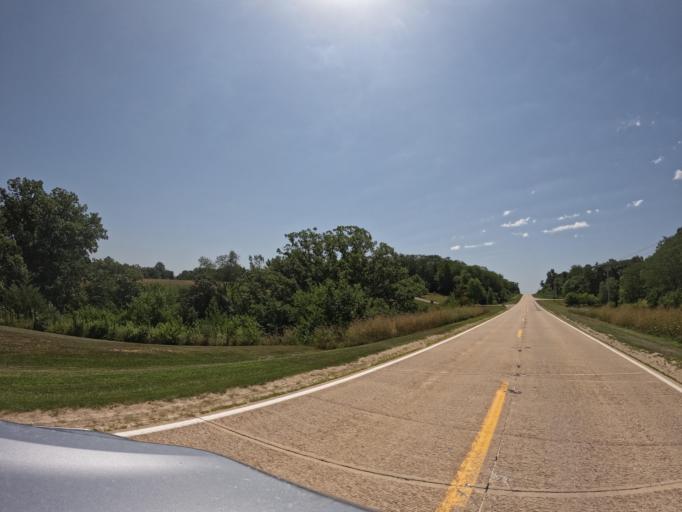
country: US
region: Iowa
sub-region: Henry County
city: Mount Pleasant
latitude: 40.9173
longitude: -91.5542
